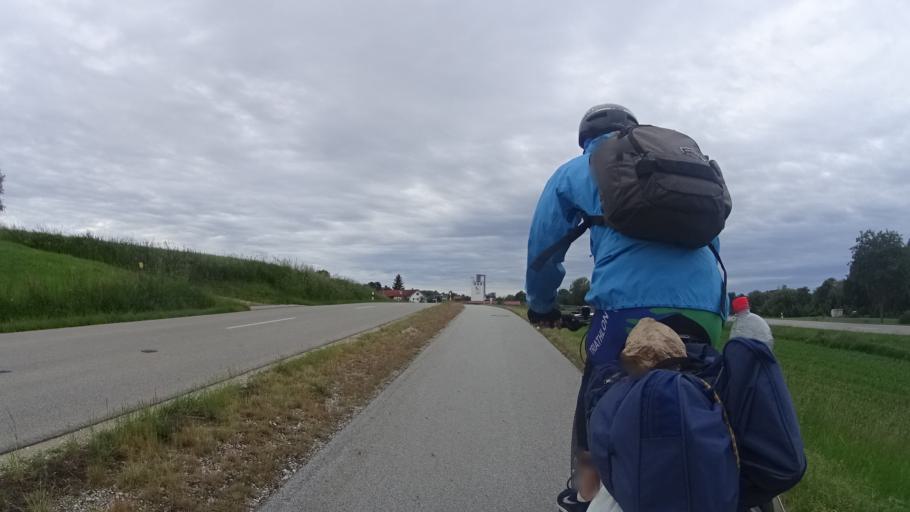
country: DE
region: Bavaria
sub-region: Lower Bavaria
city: Velden
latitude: 48.3876
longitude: 12.2903
